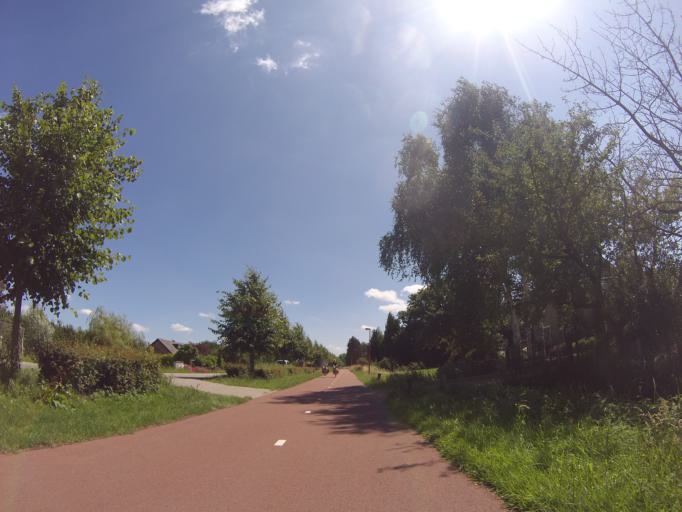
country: NL
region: Utrecht
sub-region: Gemeente Utrecht
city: Utrecht
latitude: 52.1325
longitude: 5.0948
